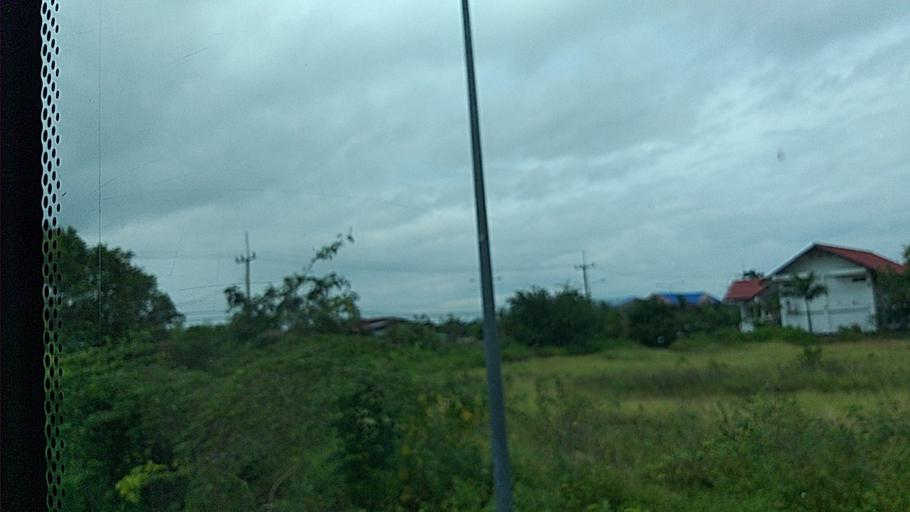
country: TH
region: Maha Sarakham
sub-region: Amphoe Borabue
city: Borabue
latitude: 16.0371
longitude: 103.1256
